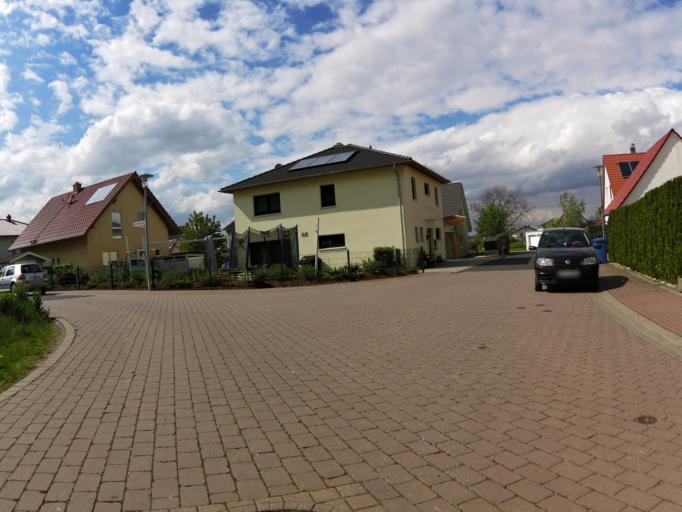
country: DE
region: Bavaria
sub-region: Regierungsbezirk Unterfranken
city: Oberpleichfeld
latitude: 49.8753
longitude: 10.0833
